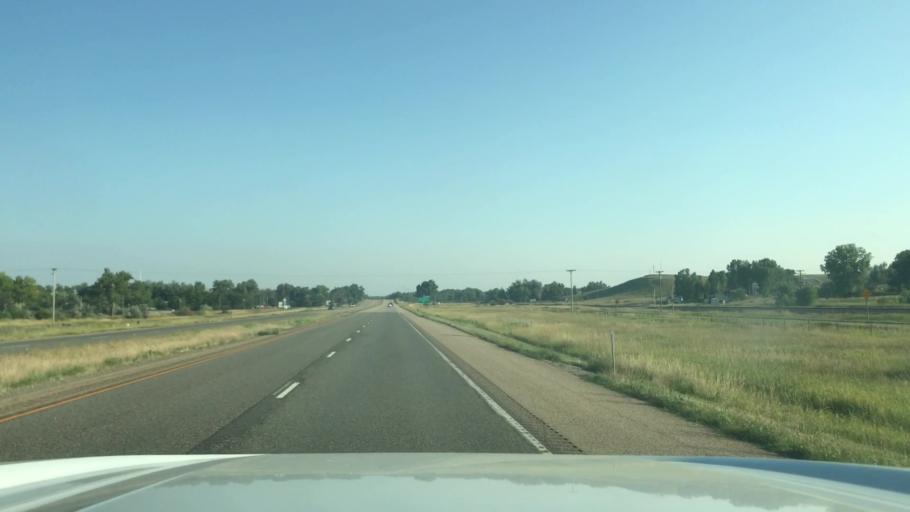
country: US
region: Montana
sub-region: Big Horn County
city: Crow Agency
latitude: 45.6103
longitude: -107.4644
